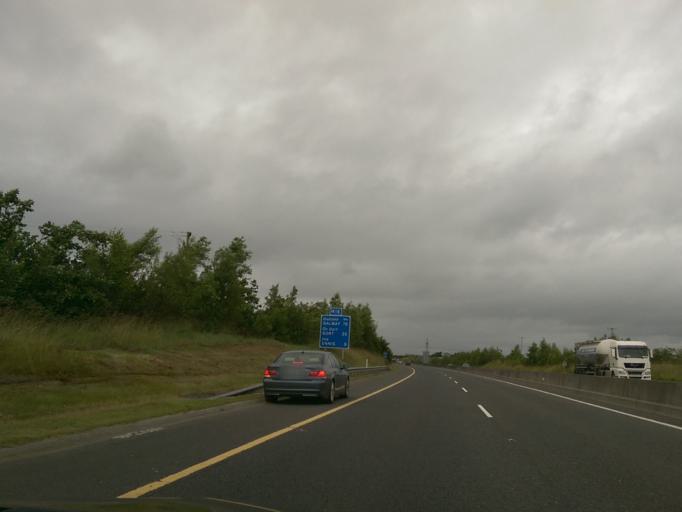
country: IE
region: Munster
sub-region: An Clar
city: Newmarket on Fergus
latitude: 52.7985
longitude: -8.9230
